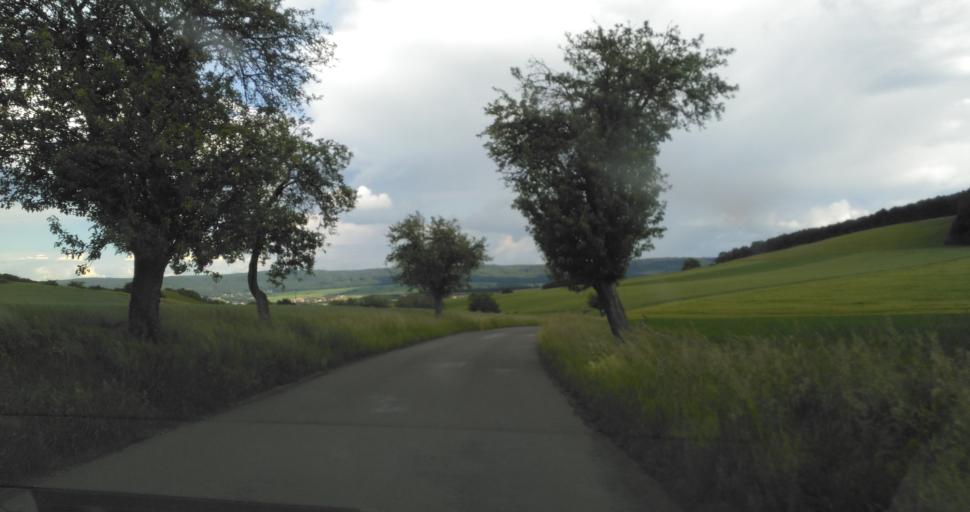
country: CZ
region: Central Bohemia
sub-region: Okres Beroun
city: Beroun
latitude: 49.9231
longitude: 14.1276
